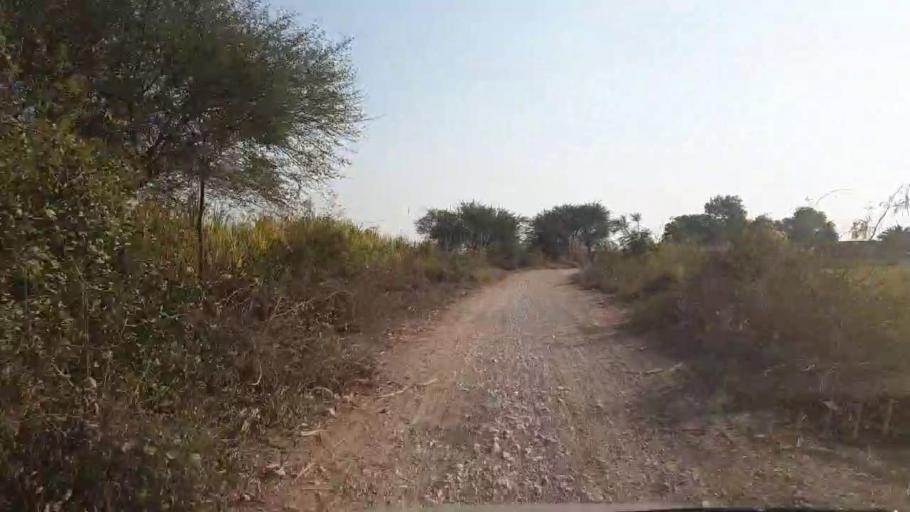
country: PK
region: Sindh
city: Chambar
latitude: 25.3146
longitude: 68.7637
